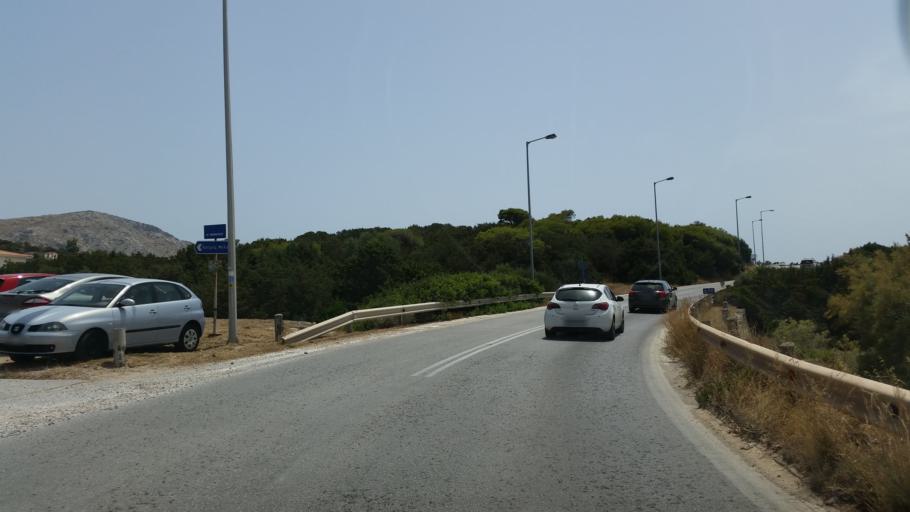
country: GR
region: Attica
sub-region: Nomarchia Anatolikis Attikis
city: Palaia Fokaia
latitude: 37.6893
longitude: 23.9388
